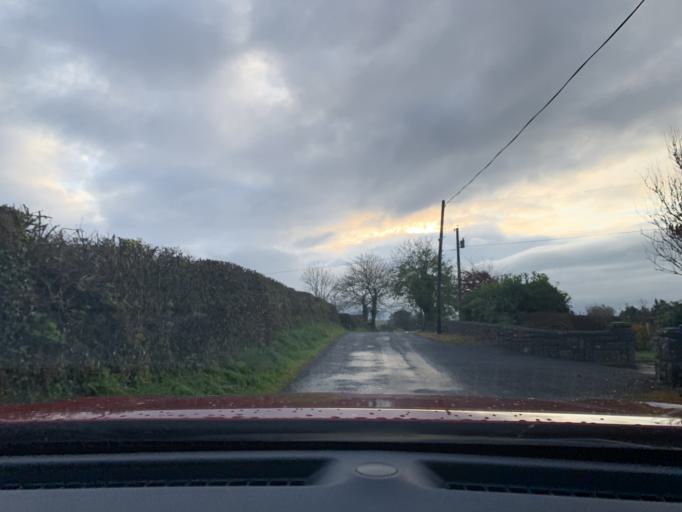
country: IE
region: Connaught
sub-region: Sligo
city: Ballymote
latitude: 54.0360
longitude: -8.5399
